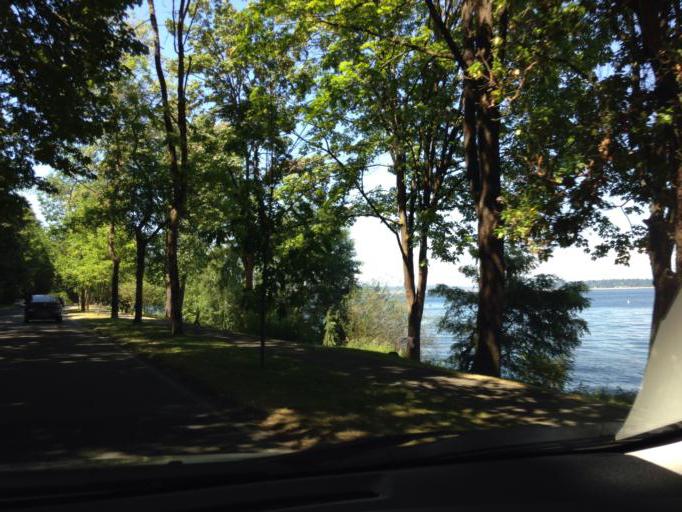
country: US
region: Washington
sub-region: King County
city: Seattle
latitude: 47.5775
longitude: -122.2832
